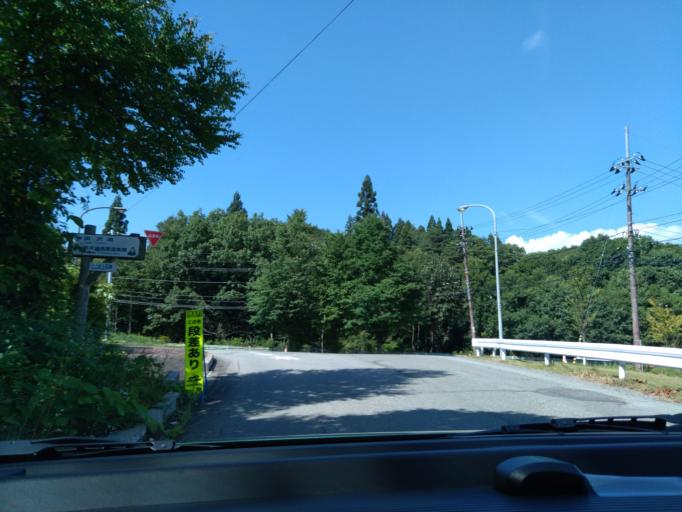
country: JP
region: Akita
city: Kakunodatemachi
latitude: 39.7345
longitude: 140.7057
